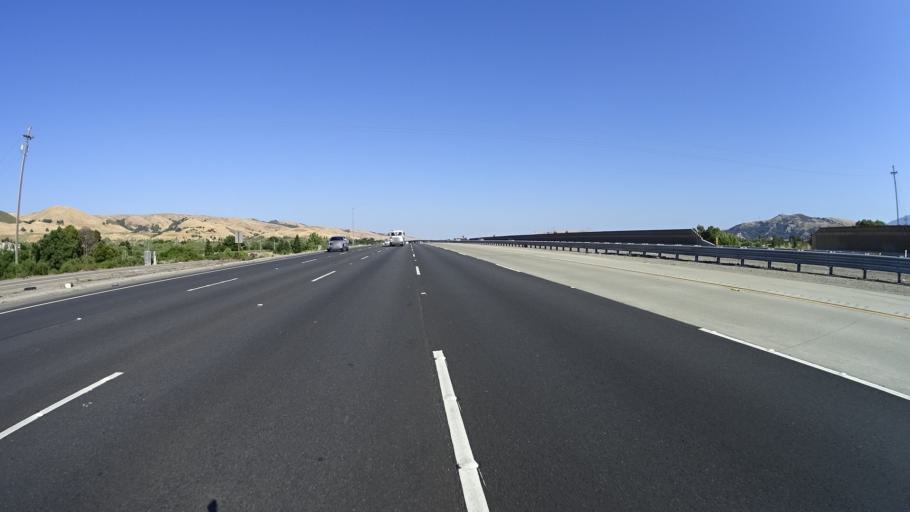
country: US
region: California
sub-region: Santa Clara County
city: Seven Trees
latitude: 37.2456
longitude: -121.7751
